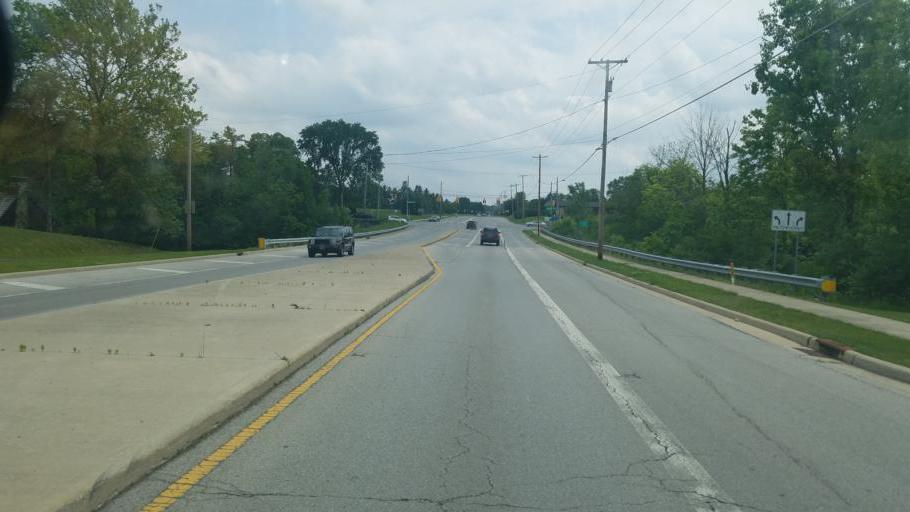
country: US
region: Ohio
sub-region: Franklin County
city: Hilliard
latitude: 40.0566
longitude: -83.1601
